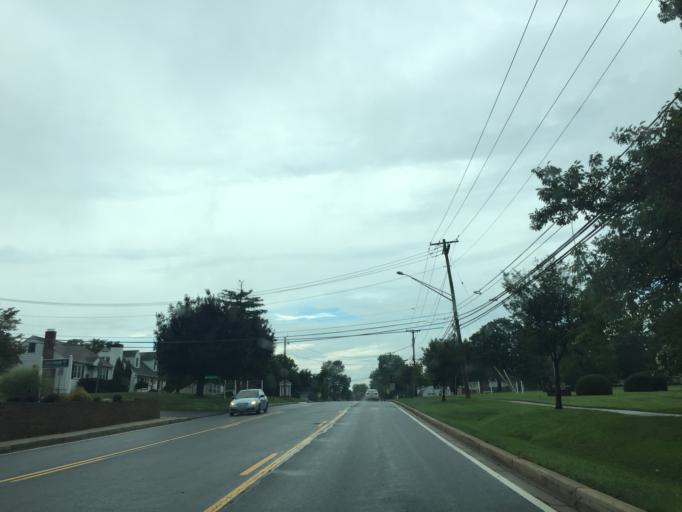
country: US
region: Maryland
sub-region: Harford County
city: South Bel Air
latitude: 39.5303
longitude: -76.3427
